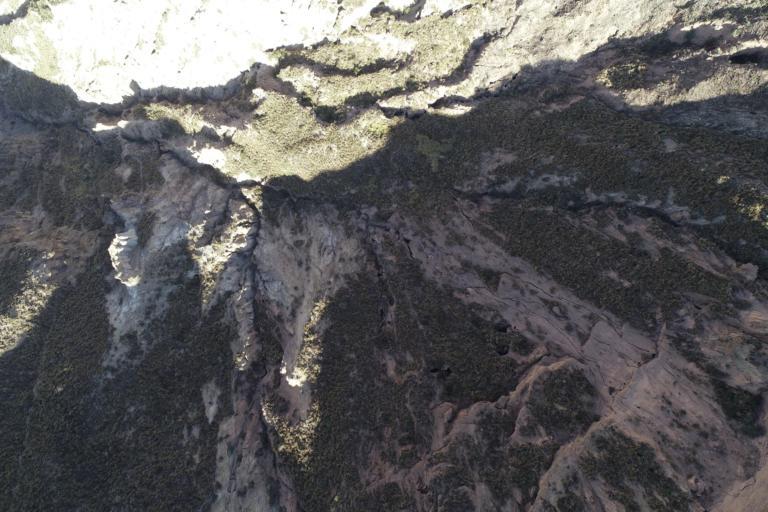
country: BO
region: La Paz
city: La Paz
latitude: -16.5513
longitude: -68.1053
